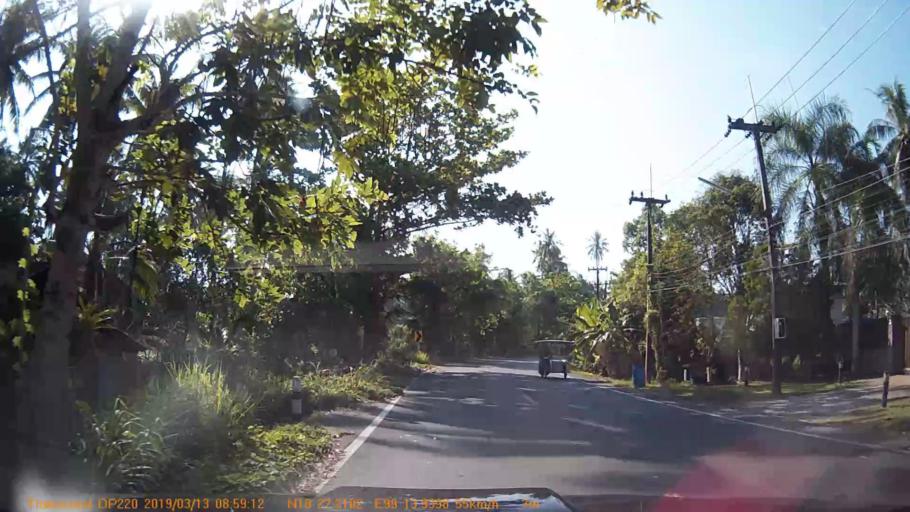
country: TH
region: Chumphon
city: Chumphon
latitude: 10.4533
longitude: 99.2325
